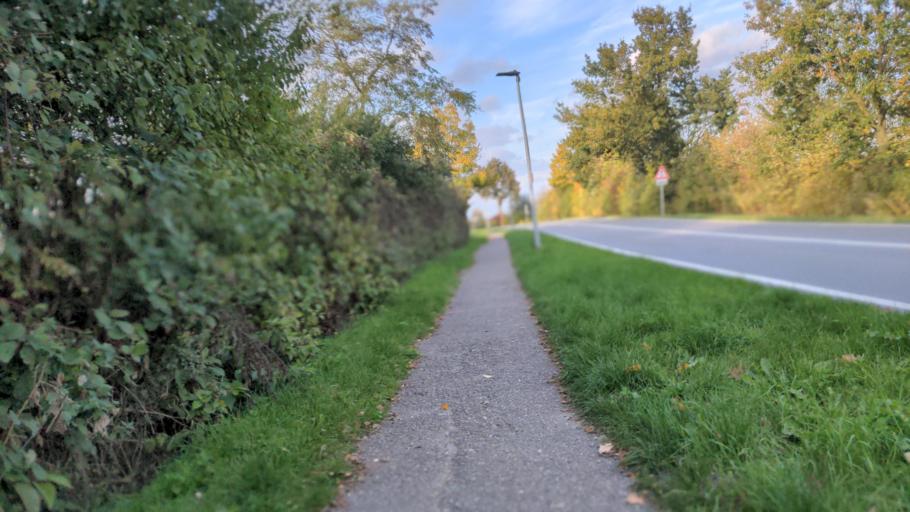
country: DE
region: Schleswig-Holstein
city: Ahrensbok
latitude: 54.0108
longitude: 10.5821
